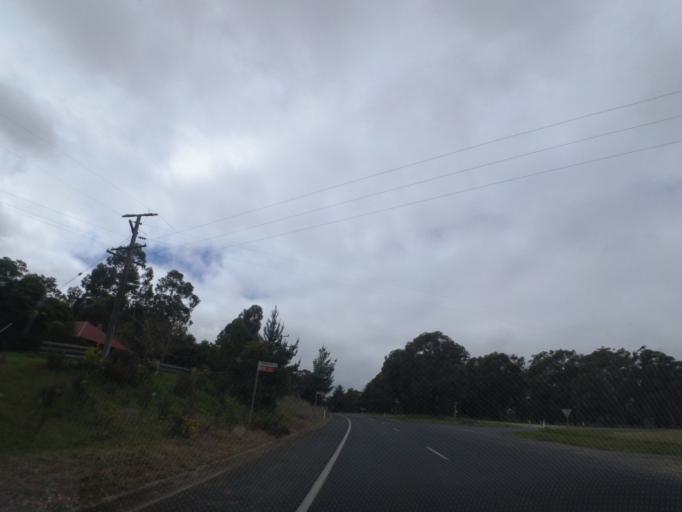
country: AU
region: Victoria
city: Brown Hill
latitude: -37.4148
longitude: 143.9349
